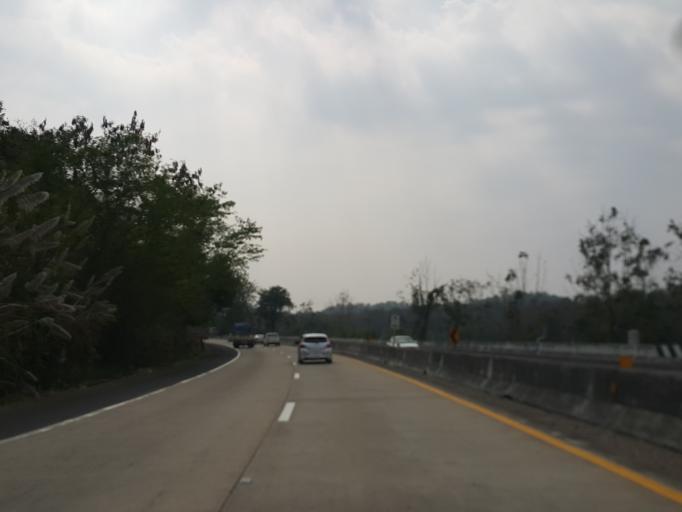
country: TH
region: Lampang
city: Hang Chat
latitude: 18.3387
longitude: 99.2470
